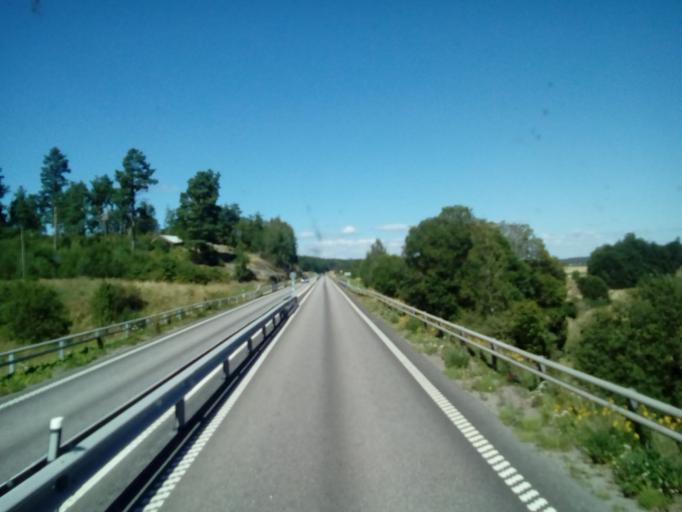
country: SE
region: OEstergoetland
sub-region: Kinda Kommun
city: Rimforsa
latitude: 58.1110
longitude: 15.6713
